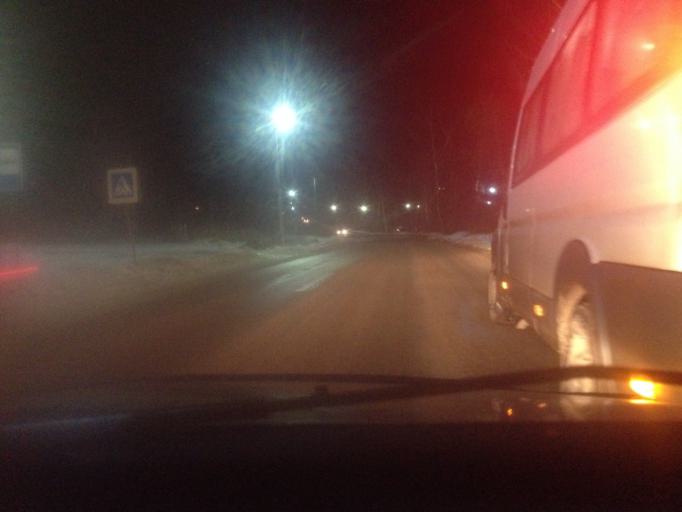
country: RU
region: Tula
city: Leninskiy
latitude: 54.2805
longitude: 37.4563
